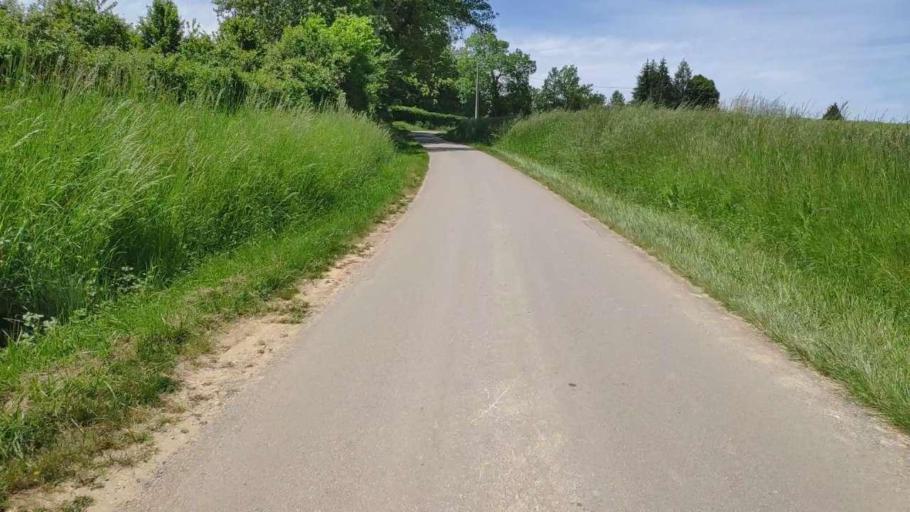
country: FR
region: Franche-Comte
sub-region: Departement du Jura
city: Bletterans
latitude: 46.7808
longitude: 5.3827
